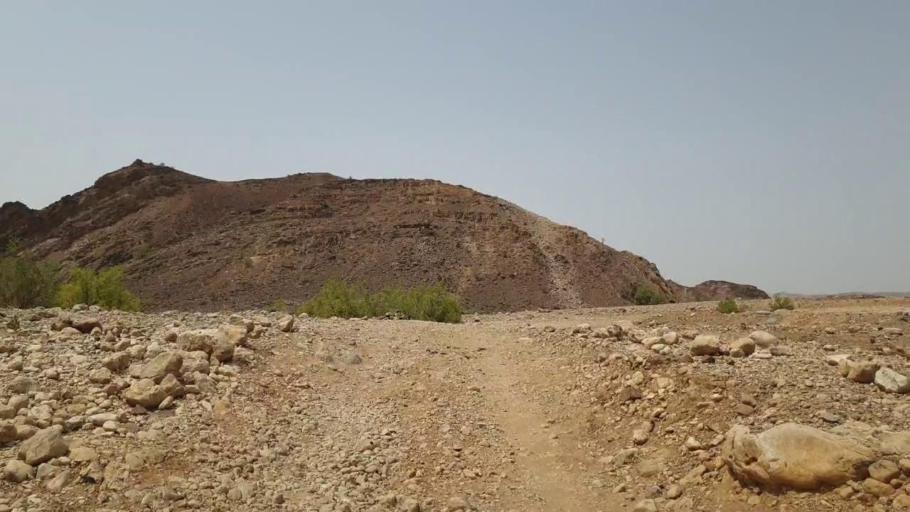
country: PK
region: Sindh
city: Sann
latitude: 25.8855
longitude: 67.9210
